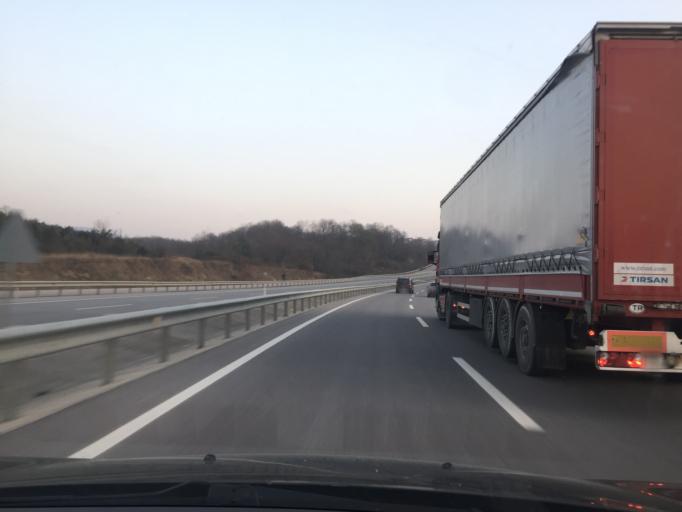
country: TR
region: Sakarya
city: Akyazi
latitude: 40.6297
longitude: 30.6411
